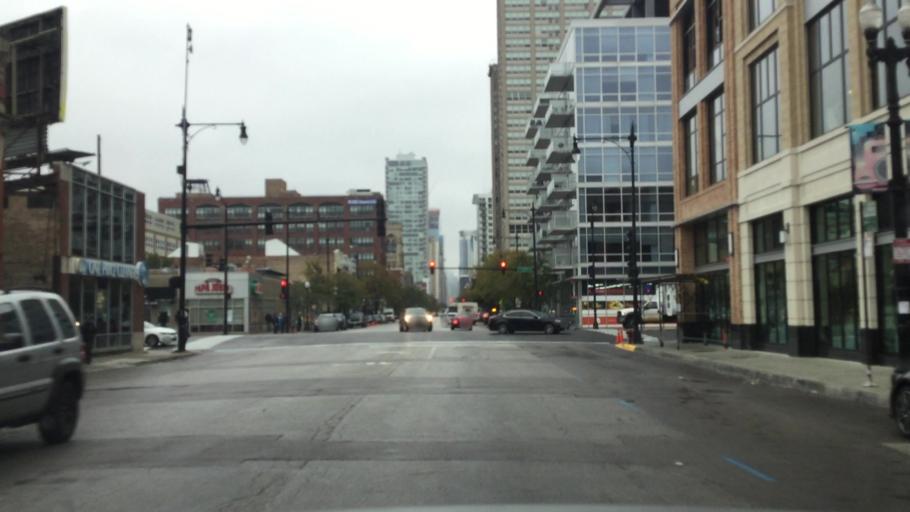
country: US
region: Illinois
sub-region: Cook County
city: Chicago
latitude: 41.8524
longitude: -87.6238
